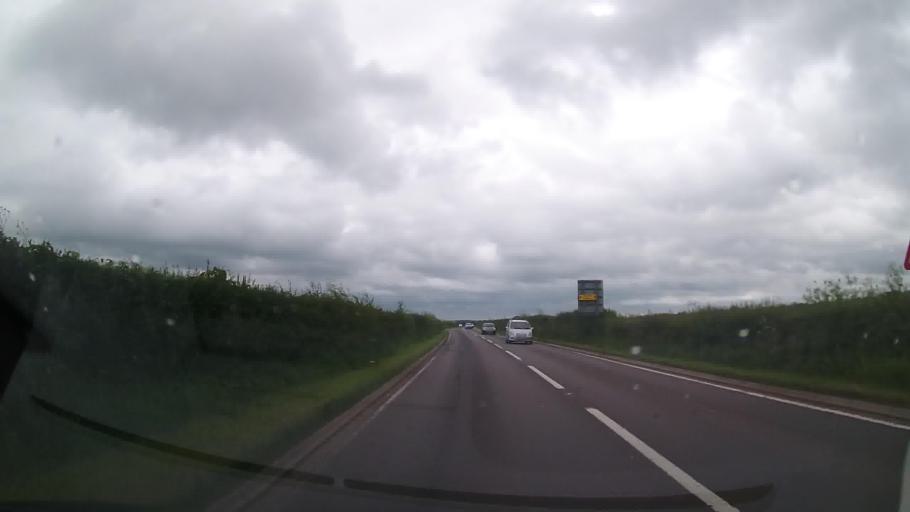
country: GB
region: England
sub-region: Shropshire
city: Prees
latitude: 52.9020
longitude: -2.6209
